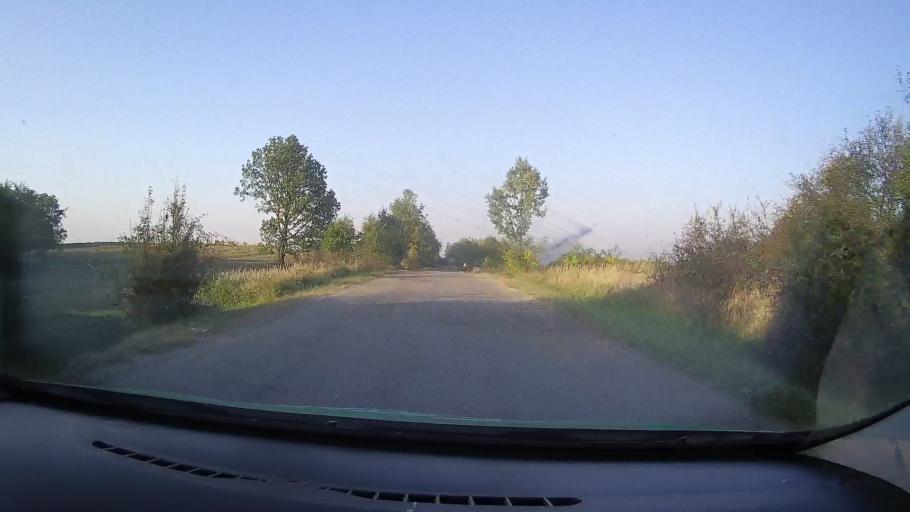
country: RO
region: Arad
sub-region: Comuna Silindia
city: Silindia
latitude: 46.3329
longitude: 21.9809
